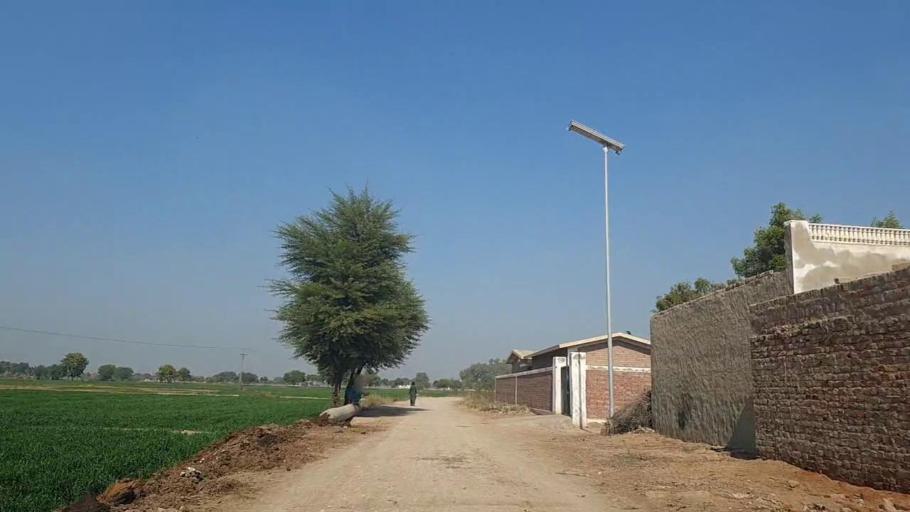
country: PK
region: Sindh
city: Nawabshah
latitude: 26.2475
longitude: 68.3384
